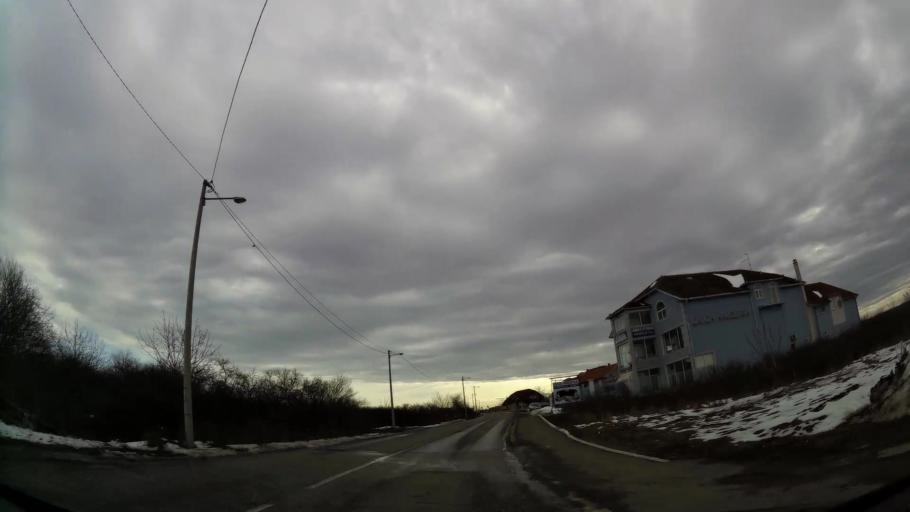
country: RS
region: Central Serbia
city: Sremcica
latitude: 44.7284
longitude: 20.3883
